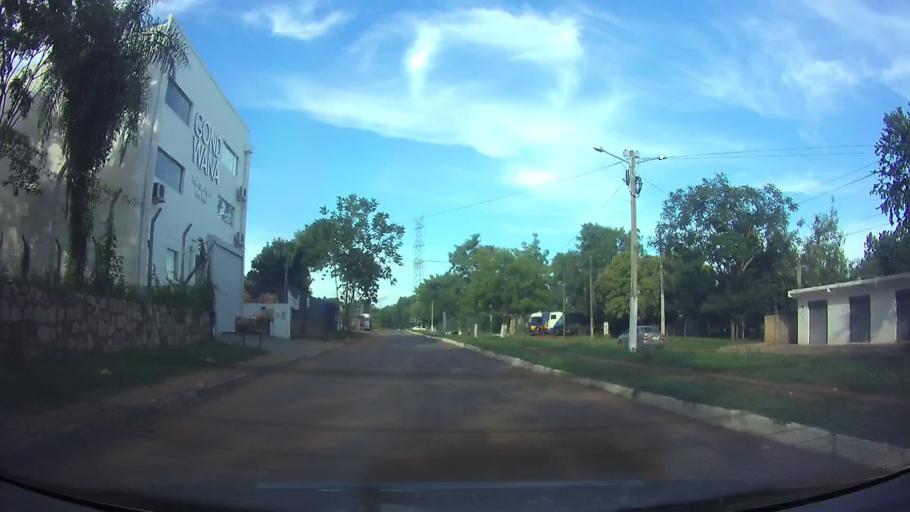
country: PY
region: Central
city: San Antonio
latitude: -25.4243
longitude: -57.5419
